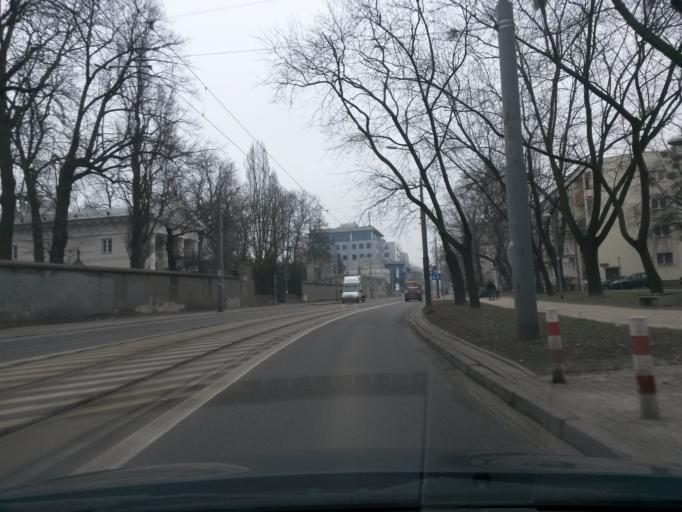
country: PL
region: Masovian Voivodeship
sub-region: Warszawa
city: Wola
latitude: 52.2421
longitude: 20.9699
